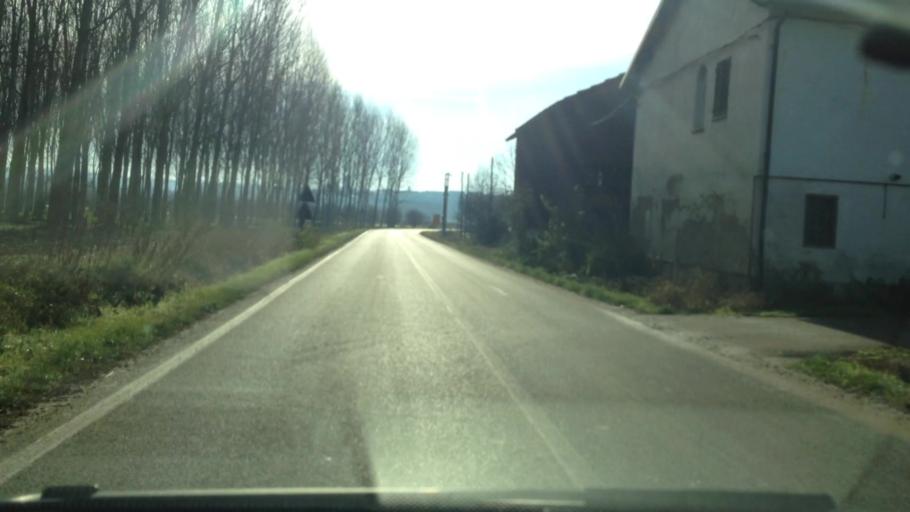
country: IT
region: Piedmont
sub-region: Provincia di Alessandria
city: Masio
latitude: 44.8842
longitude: 8.4103
